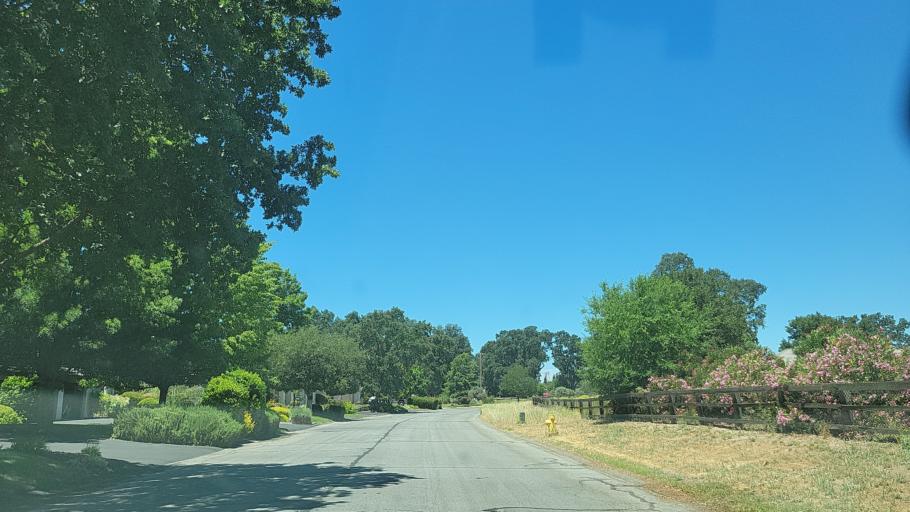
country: US
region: California
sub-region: San Luis Obispo County
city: Atascadero
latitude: 35.5117
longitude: -120.6689
